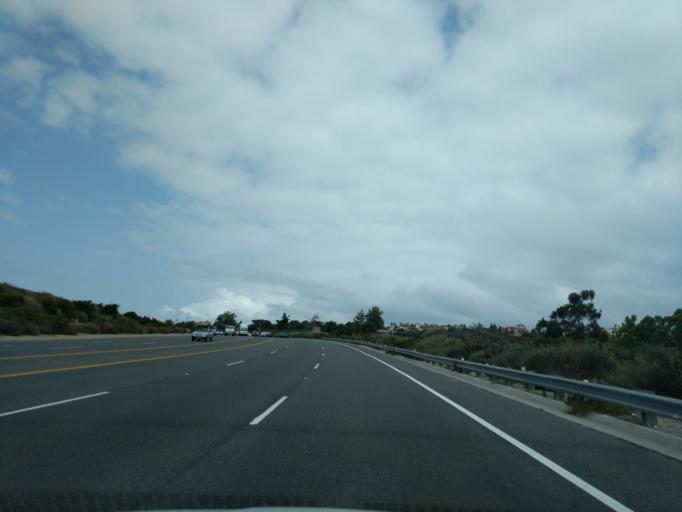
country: US
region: California
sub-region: Orange County
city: San Joaquin Hills
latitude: 33.5766
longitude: -117.8402
